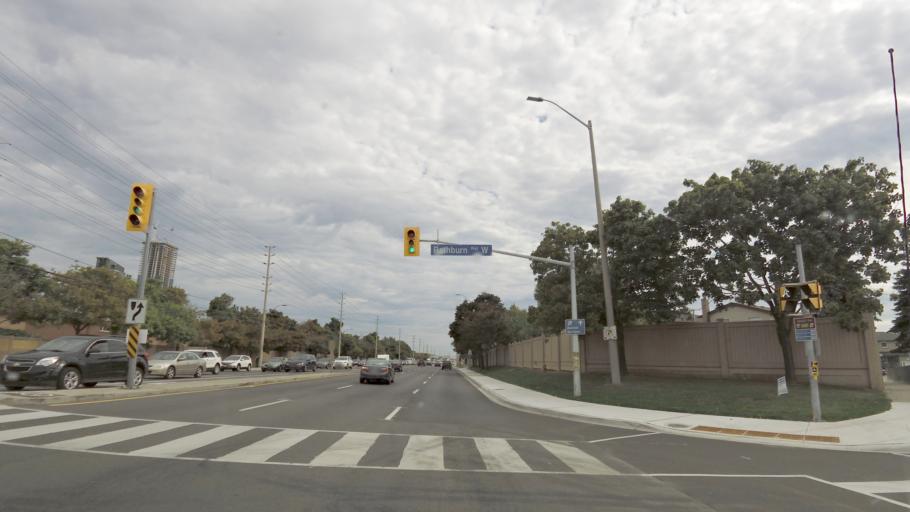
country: CA
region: Ontario
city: Mississauga
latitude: 43.5825
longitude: -79.6559
